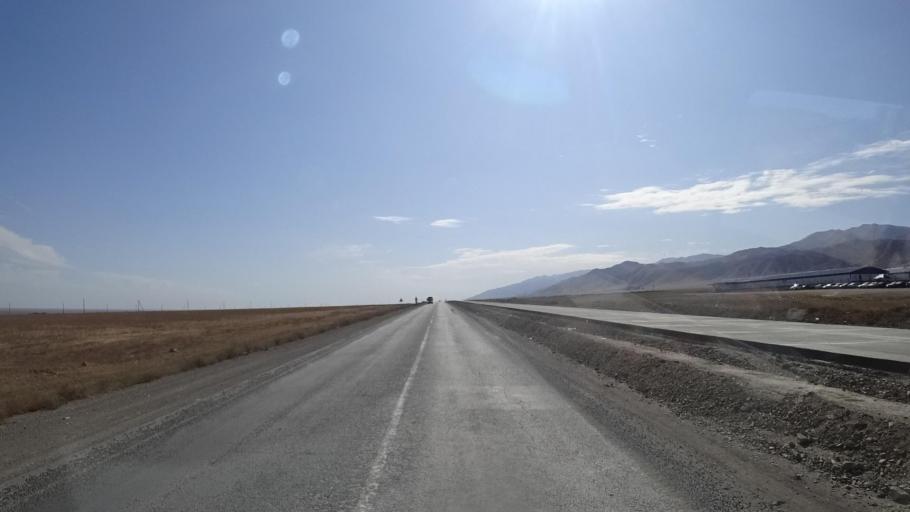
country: KG
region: Chuy
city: Ivanovka
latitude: 43.3904
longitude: 75.1418
